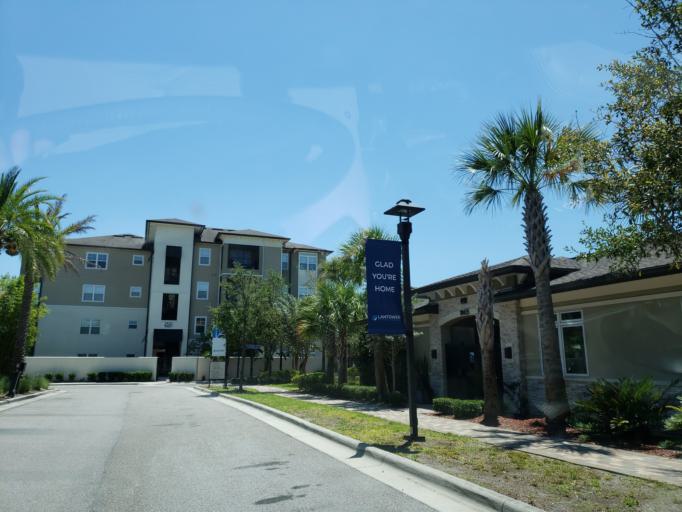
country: US
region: Florida
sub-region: Hillsborough County
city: Progress Village
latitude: 27.9255
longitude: -82.3356
